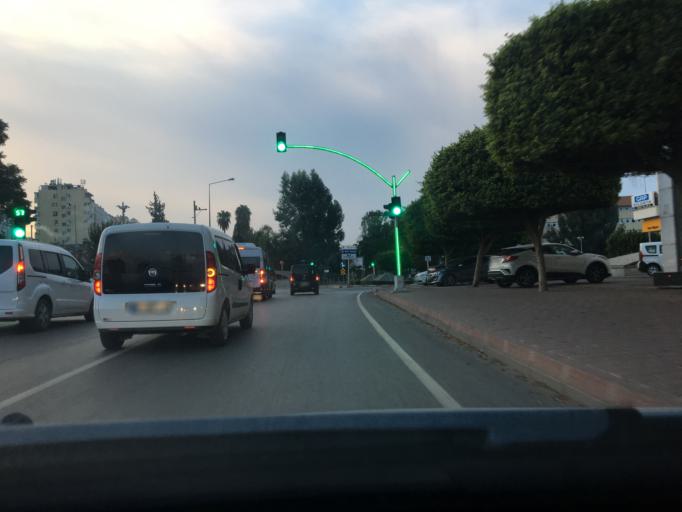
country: TR
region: Adana
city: Adana
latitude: 37.0021
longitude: 35.3131
